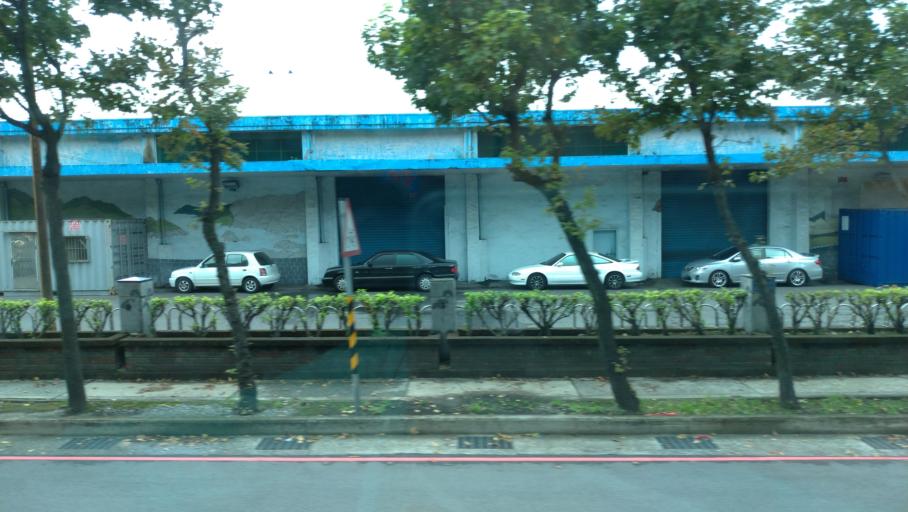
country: TW
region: Taiwan
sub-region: Keelung
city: Keelung
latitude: 25.1374
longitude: 121.7486
